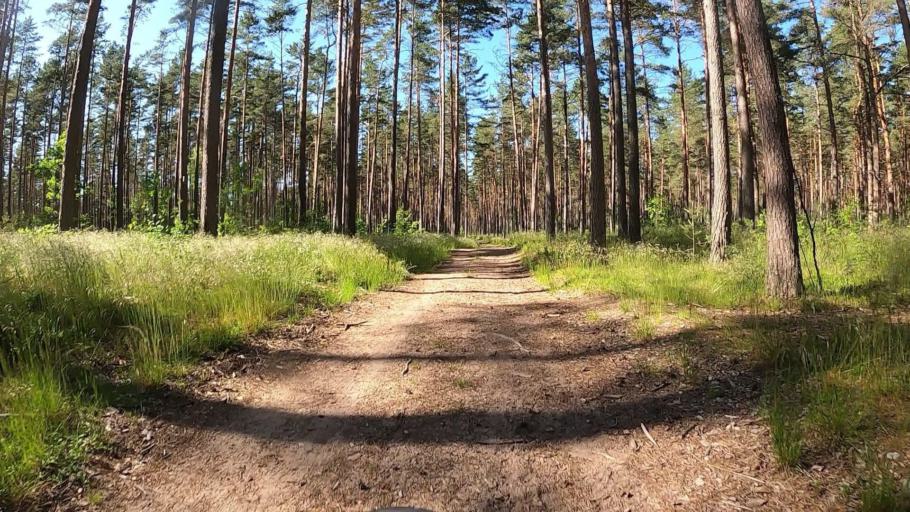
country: LV
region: Riga
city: Bergi
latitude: 57.0139
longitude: 24.2538
